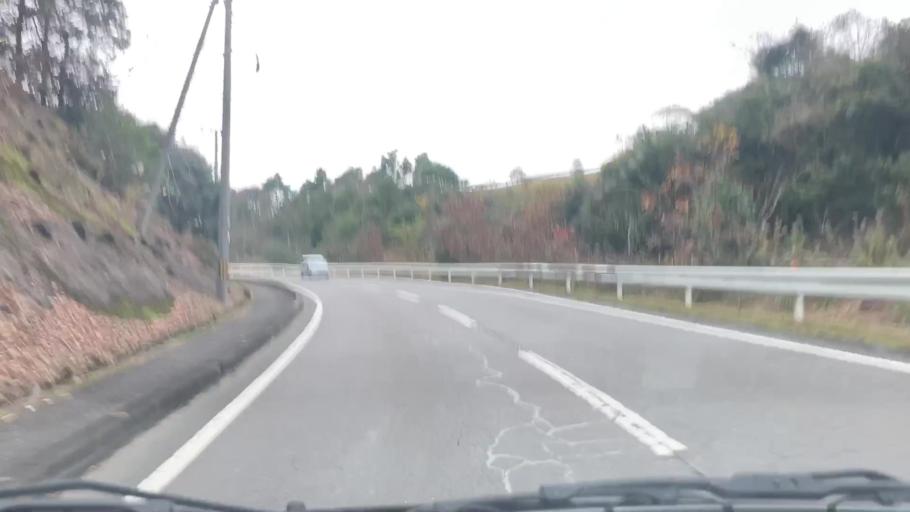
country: JP
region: Saga Prefecture
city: Ureshinomachi-shimojuku
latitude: 33.1133
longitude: 129.9760
